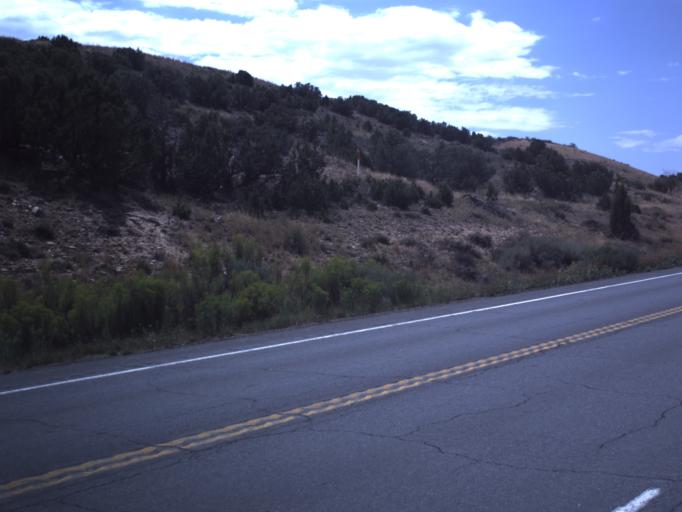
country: US
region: Utah
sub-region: Duchesne County
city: Duchesne
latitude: 40.1715
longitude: -110.3419
